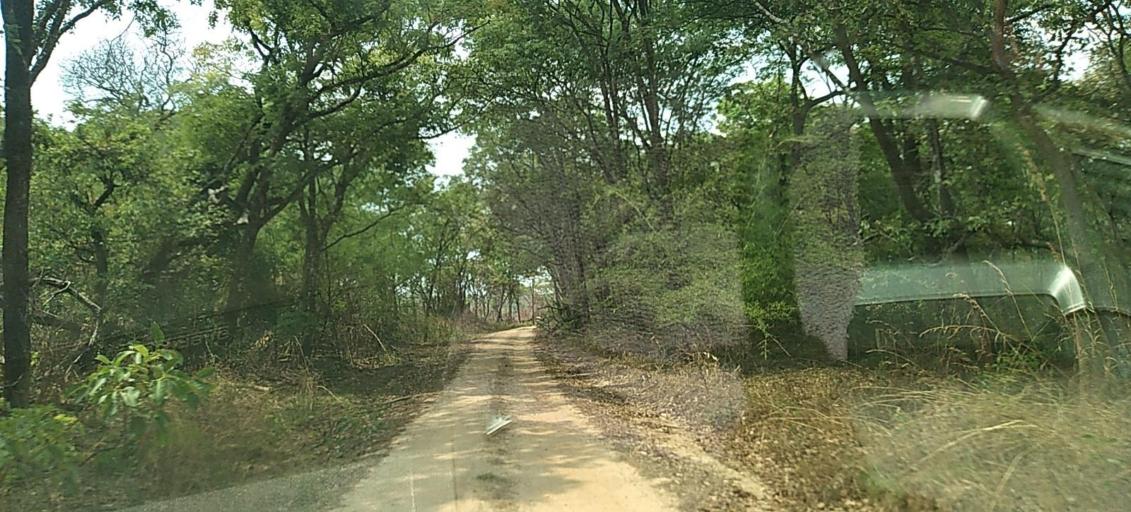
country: ZM
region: Copperbelt
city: Chingola
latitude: -12.7464
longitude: 27.7249
